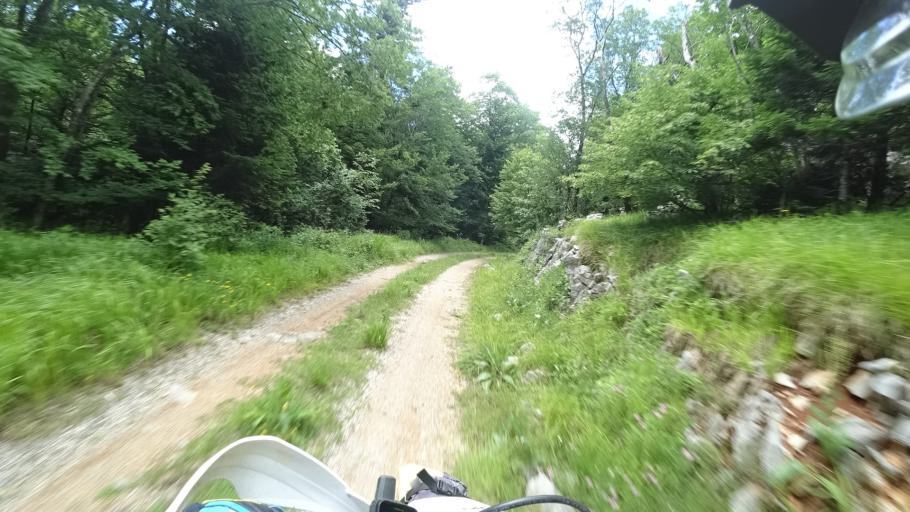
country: HR
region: Primorsko-Goranska
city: Bribir
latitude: 45.2148
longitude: 14.7489
